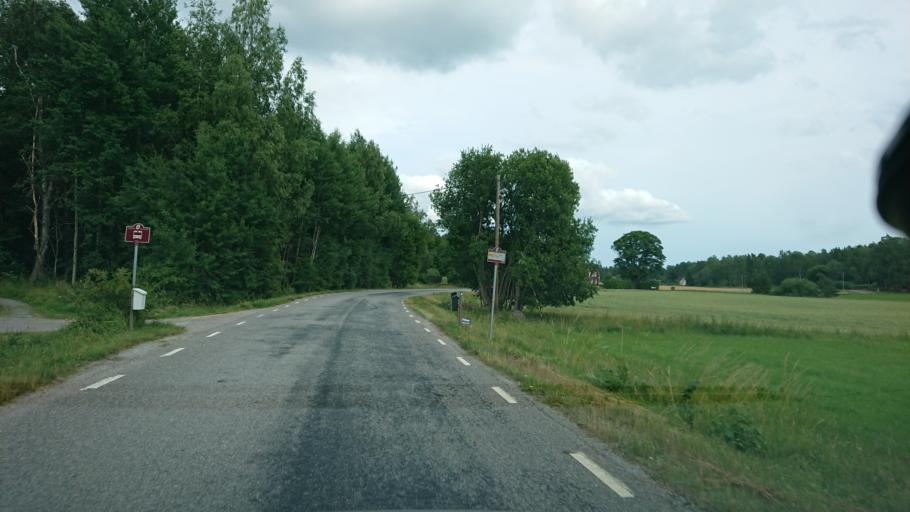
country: SE
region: Uppsala
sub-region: Osthammars Kommun
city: Bjorklinge
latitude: 60.0034
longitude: 17.4604
